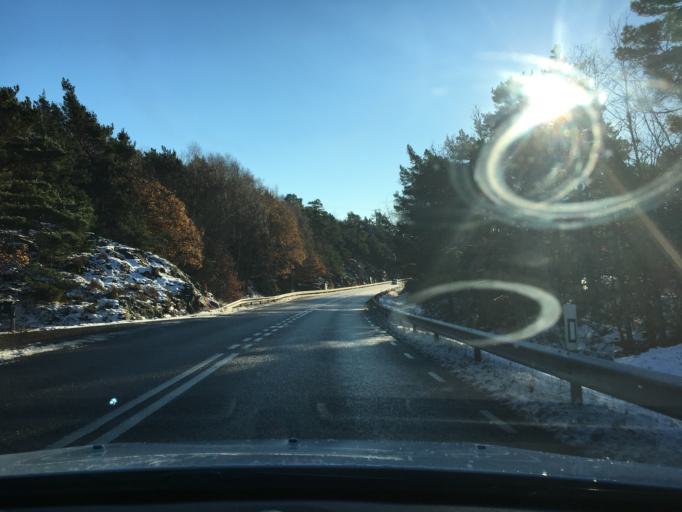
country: SE
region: Vaestra Goetaland
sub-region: Tjorns Kommun
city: Myggenas
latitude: 58.0792
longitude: 11.6961
